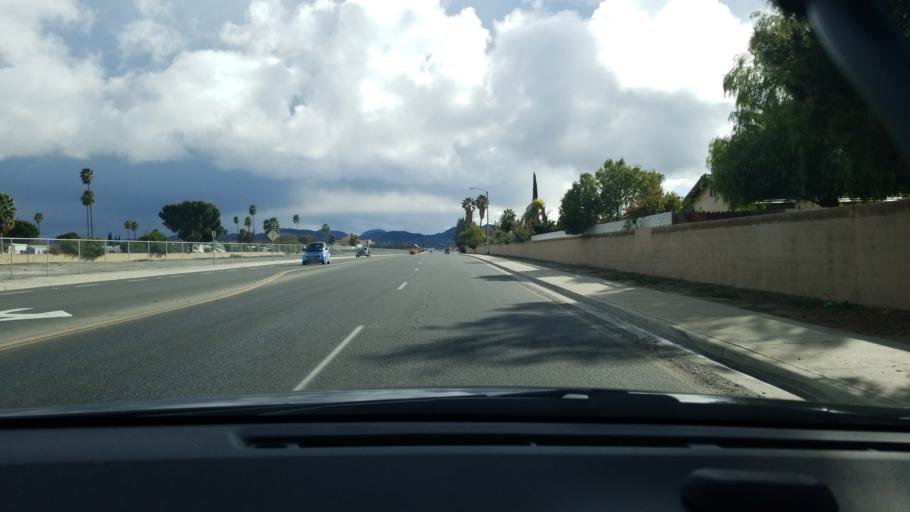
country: US
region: California
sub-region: Riverside County
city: Hemet
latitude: 33.7507
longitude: -117.0155
